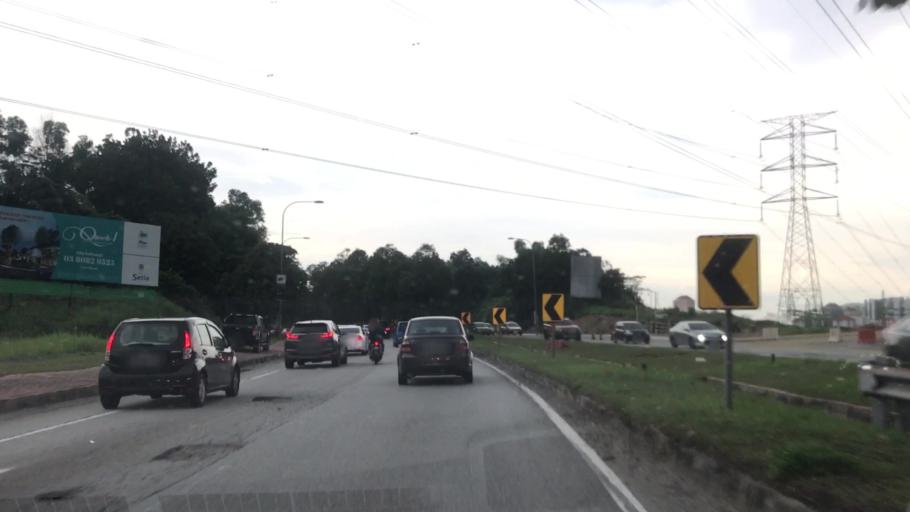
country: MY
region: Selangor
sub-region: Petaling
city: Petaling Jaya
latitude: 3.0555
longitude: 101.6664
